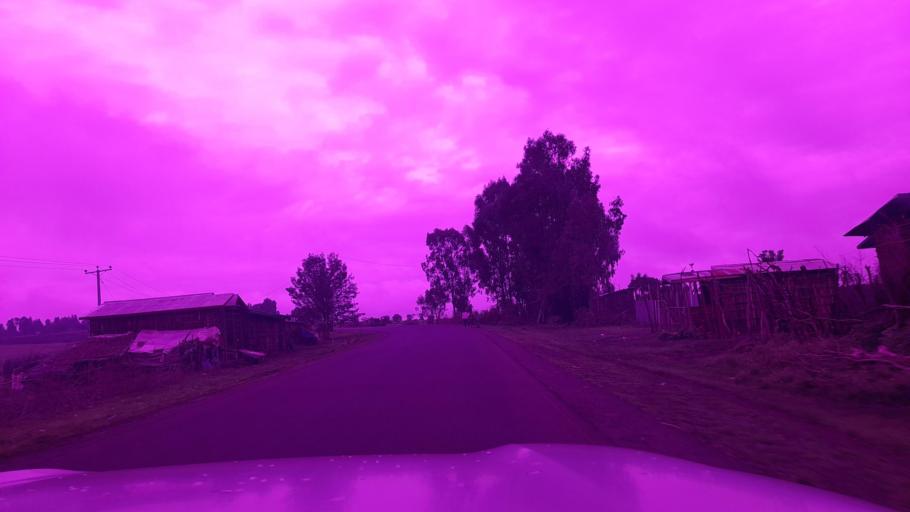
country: ET
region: Oromiya
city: Waliso
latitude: 8.2739
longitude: 37.6721
